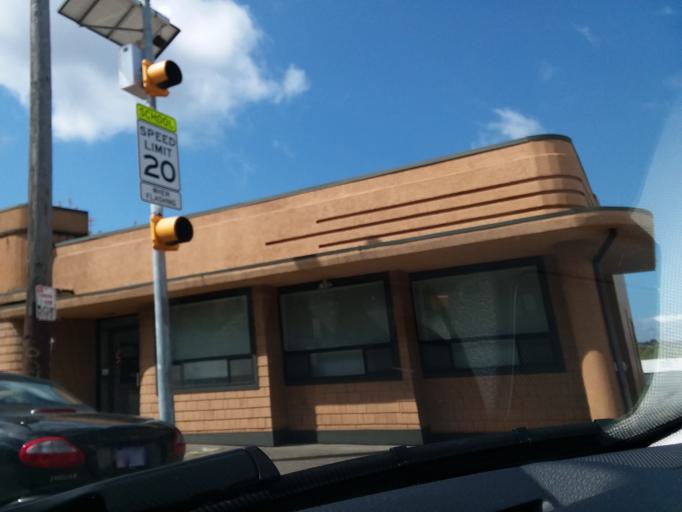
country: US
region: Washington
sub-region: King County
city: Seattle
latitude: 47.6441
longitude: -122.3260
